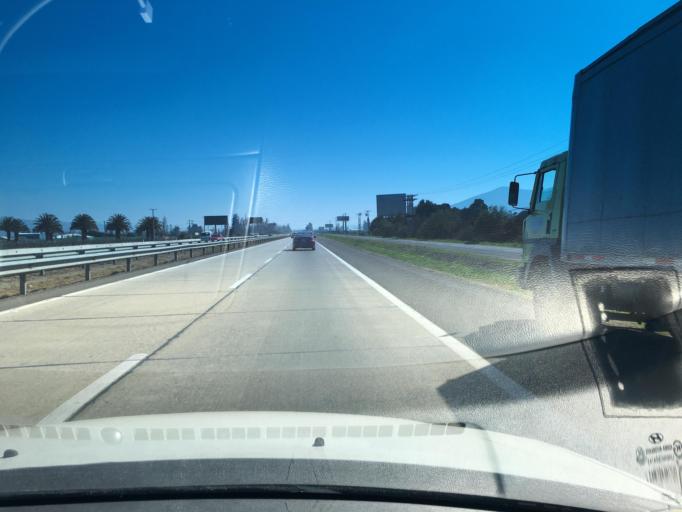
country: CL
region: Valparaiso
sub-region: Provincia de Marga Marga
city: Villa Alemana
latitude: -33.3512
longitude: -71.3427
